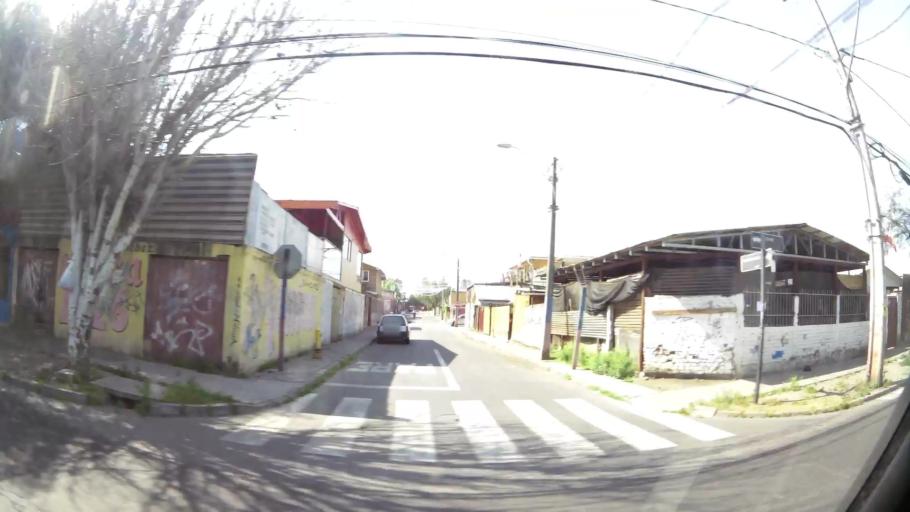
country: CL
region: Santiago Metropolitan
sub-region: Provincia de Santiago
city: Lo Prado
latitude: -33.4401
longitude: -70.7684
